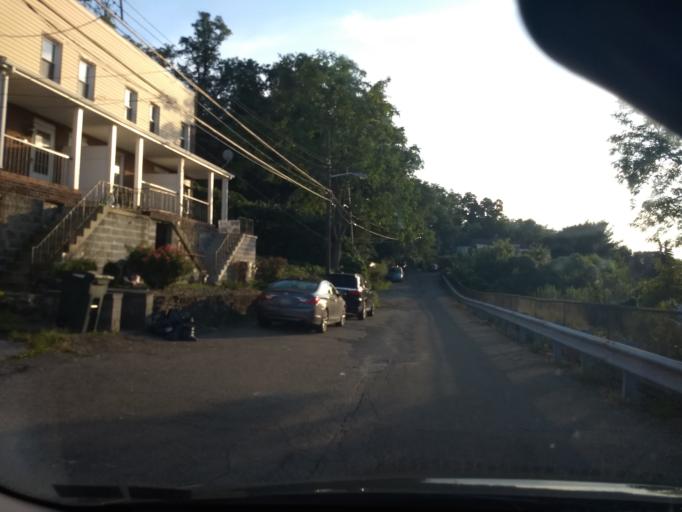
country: US
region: Pennsylvania
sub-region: Allegheny County
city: Bloomfield
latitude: 40.4560
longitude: -79.9621
